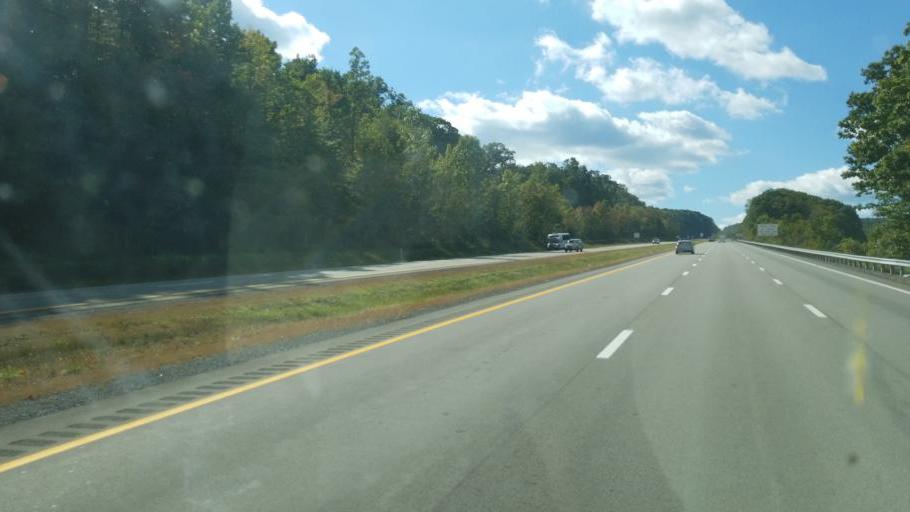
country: US
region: West Virginia
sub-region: Monongalia County
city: Cheat Lake
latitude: 39.6543
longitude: -79.7419
